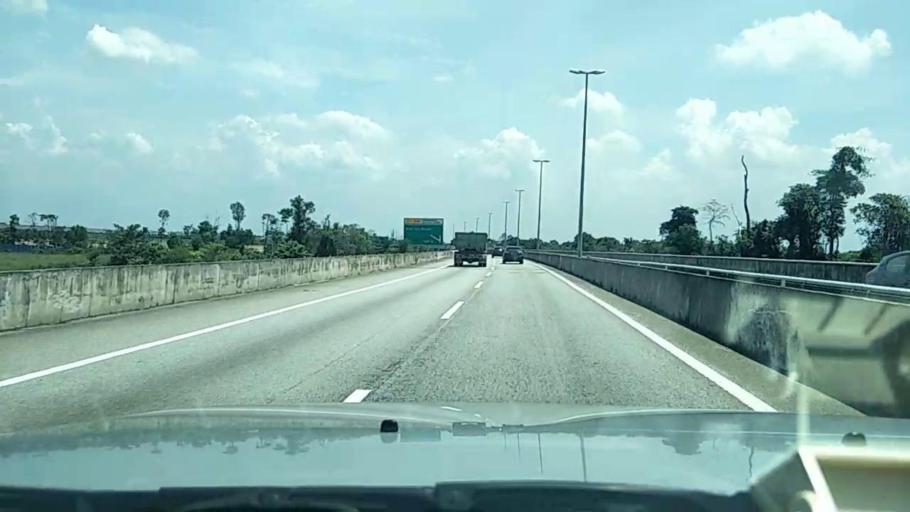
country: MY
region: Putrajaya
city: Putrajaya
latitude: 2.9467
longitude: 101.6379
